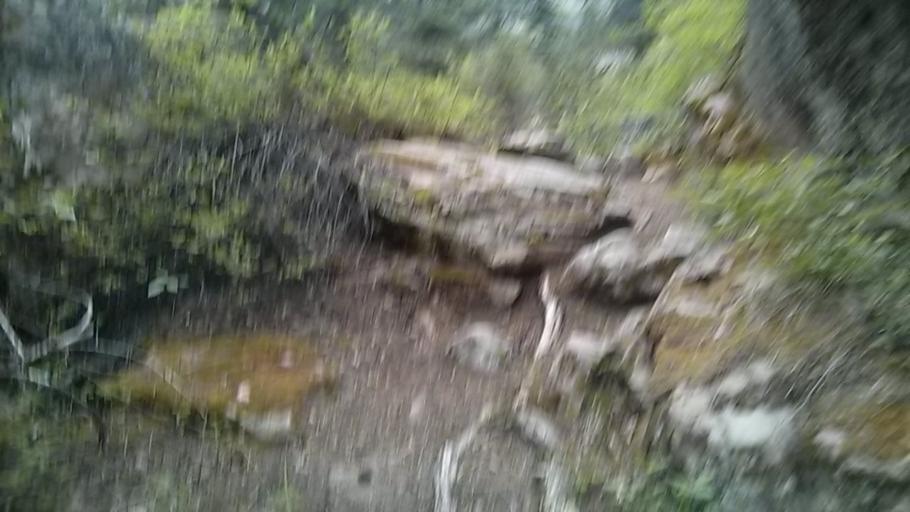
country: US
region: Utah
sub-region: Wayne County
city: Loa
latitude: 37.9601
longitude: -111.6514
